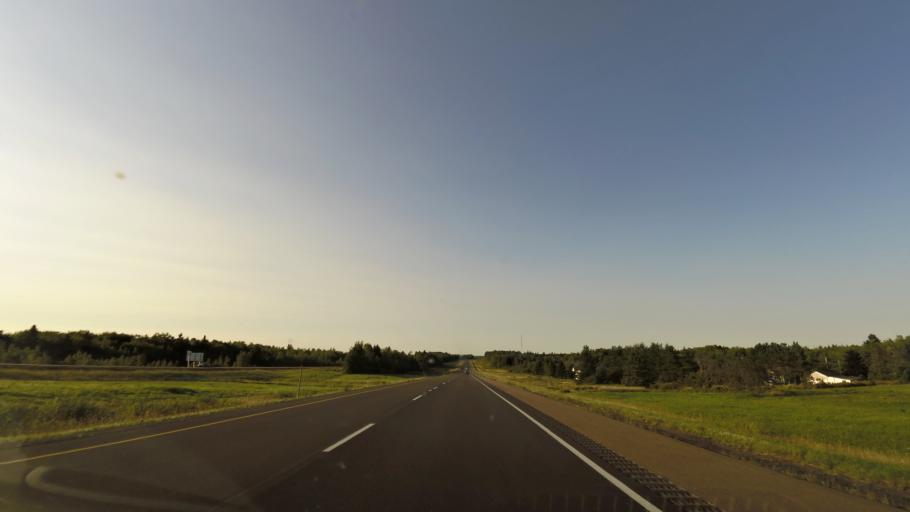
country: CA
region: New Brunswick
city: Dieppe
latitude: 46.0676
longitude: -64.5893
